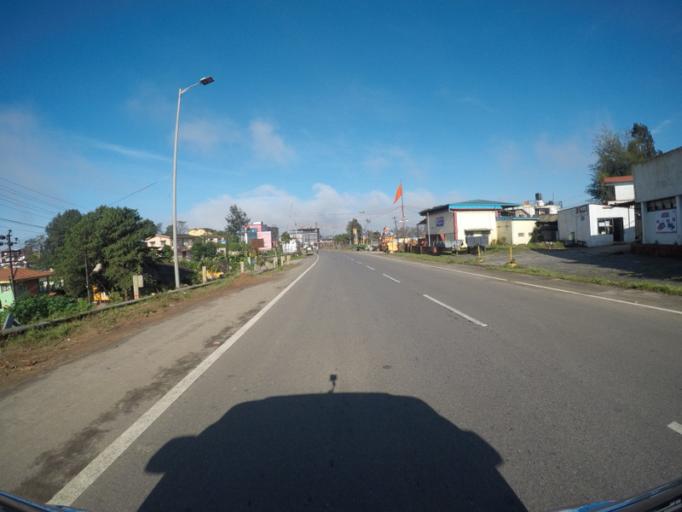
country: IN
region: Karnataka
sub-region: Kodagu
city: Madikeri
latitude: 12.4151
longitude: 75.7482
